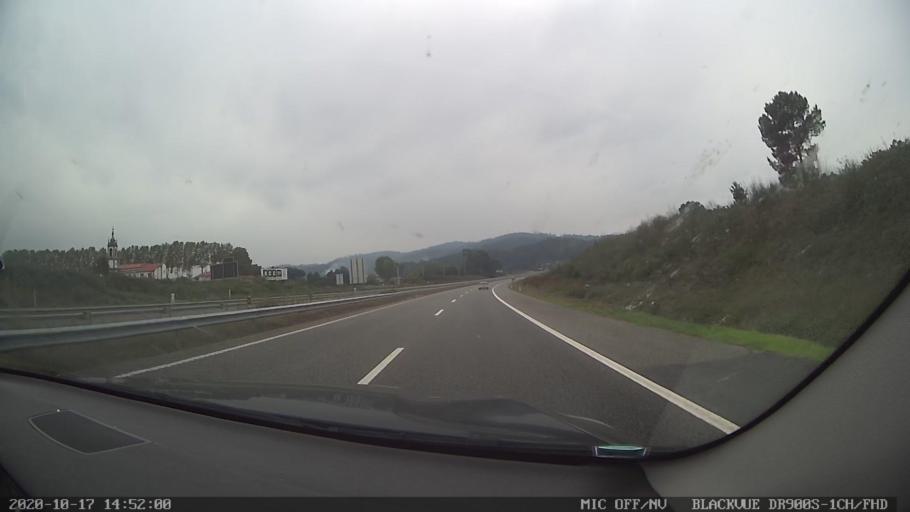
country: PT
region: Braga
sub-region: Barcelos
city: Barcelos
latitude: 41.5067
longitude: -8.6221
